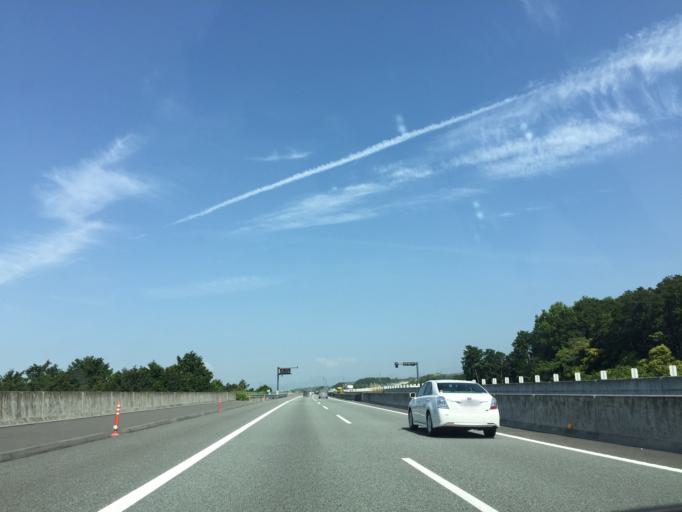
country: JP
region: Shizuoka
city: Fuji
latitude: 35.1795
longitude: 138.7319
